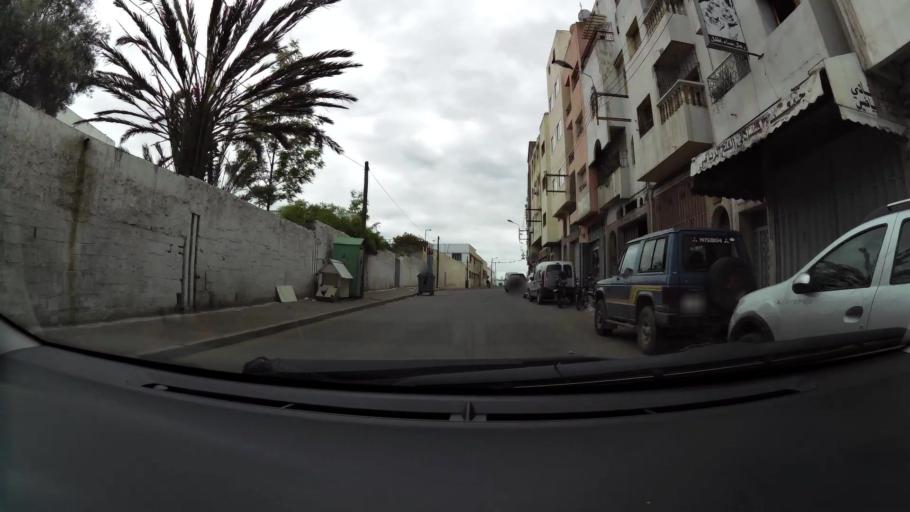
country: MA
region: Grand Casablanca
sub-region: Casablanca
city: Casablanca
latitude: 33.5844
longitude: -7.5487
